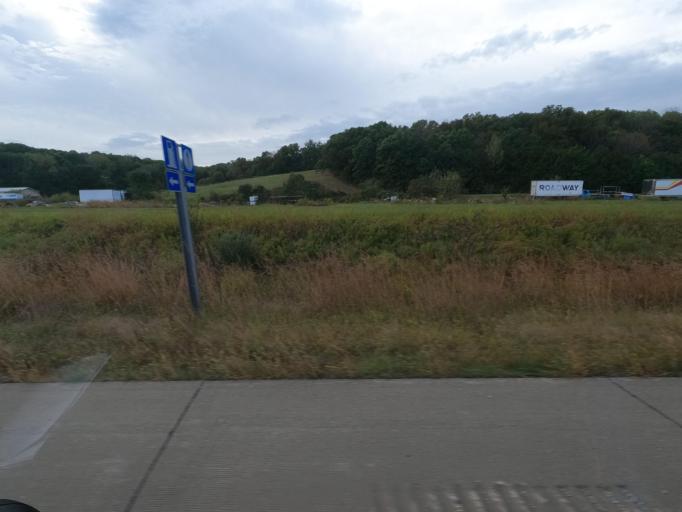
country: US
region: Missouri
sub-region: Clark County
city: Kahoka
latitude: 40.4558
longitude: -91.5694
